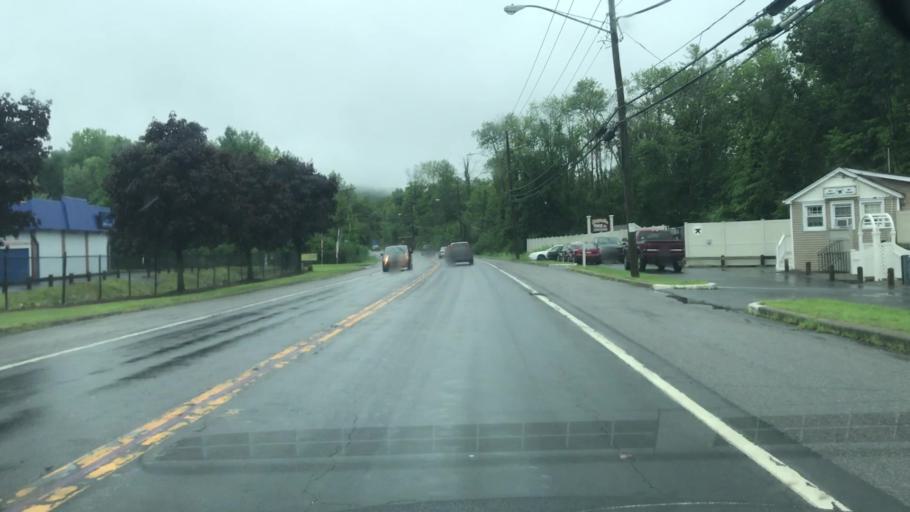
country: US
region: New York
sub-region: Putnam County
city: Mahopac
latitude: 41.3545
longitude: -73.7475
